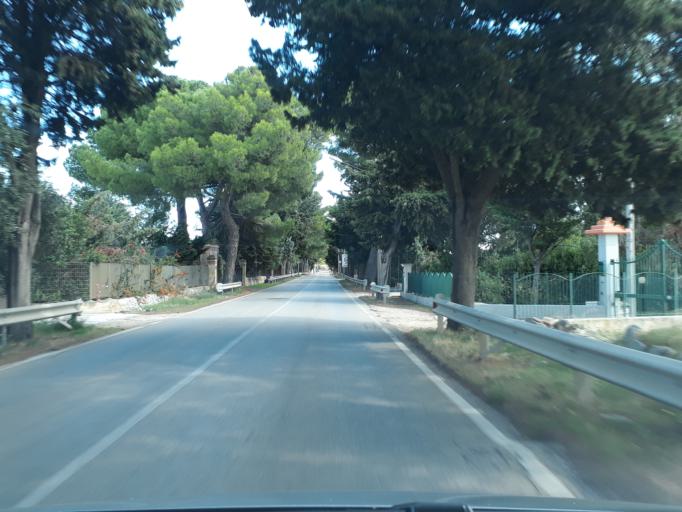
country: IT
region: Apulia
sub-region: Provincia di Bari
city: Rutigliano
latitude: 41.0312
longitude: 17.0422
